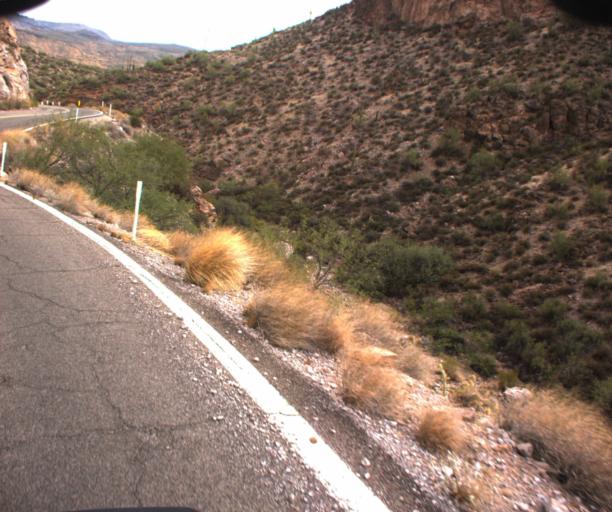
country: US
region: Arizona
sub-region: Pinal County
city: Apache Junction
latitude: 33.5321
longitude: -111.3795
